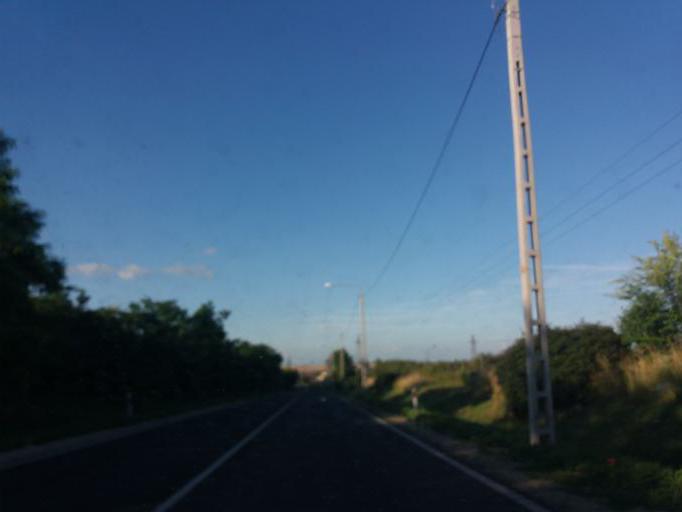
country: HU
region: Fejer
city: Baracska
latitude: 47.2767
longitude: 18.7443
